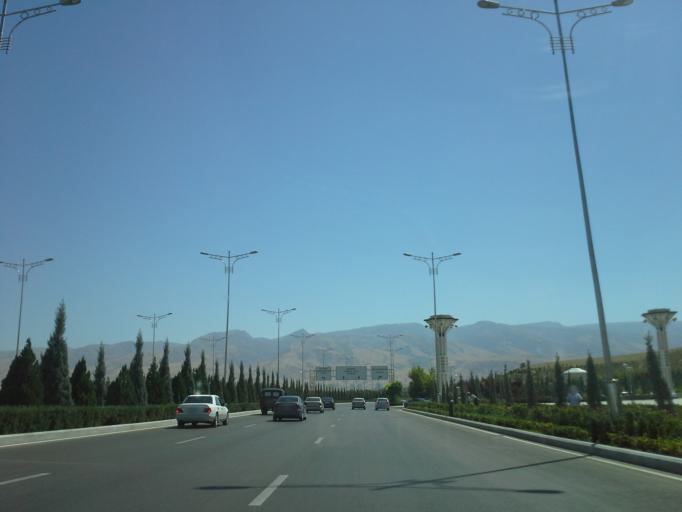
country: TM
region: Ahal
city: Ashgabat
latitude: 37.9345
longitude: 58.3204
